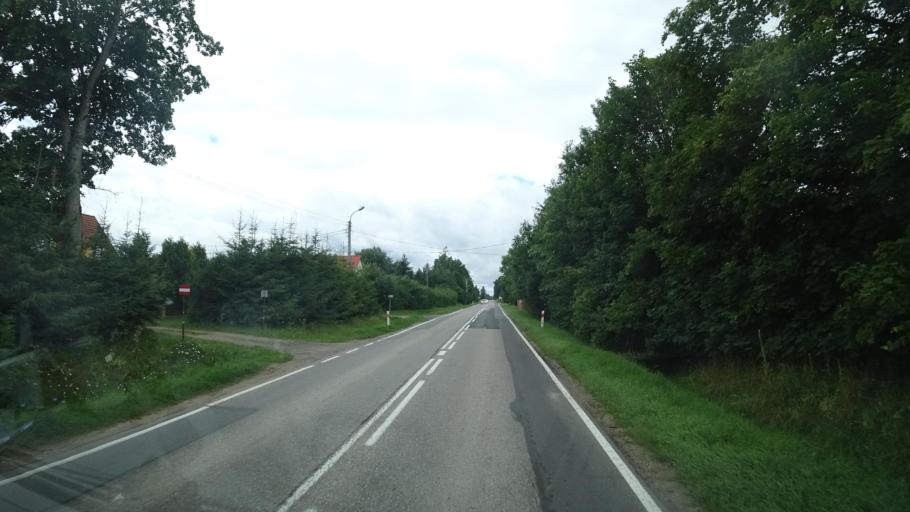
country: PL
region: Warmian-Masurian Voivodeship
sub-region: Powiat olecki
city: Olecko
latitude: 54.0709
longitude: 22.4781
